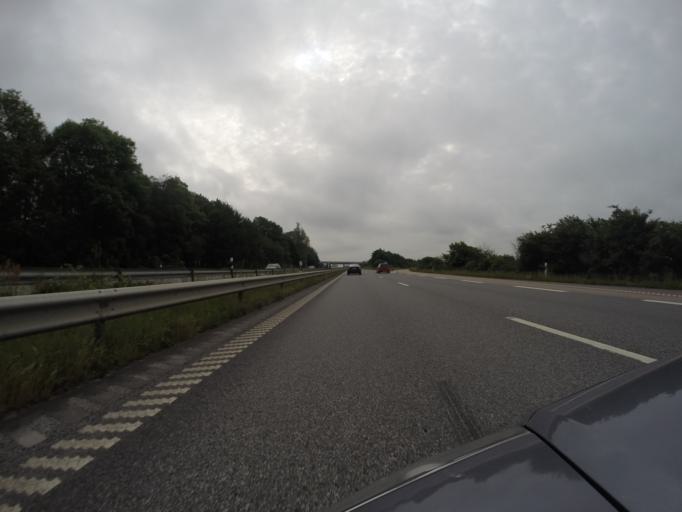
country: SE
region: Skane
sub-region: Kavlinge Kommun
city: Loddekopinge
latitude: 55.7463
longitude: 13.0251
